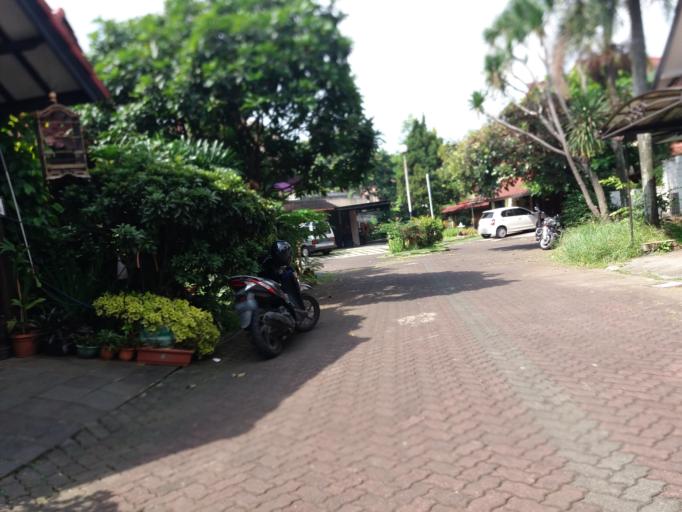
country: ID
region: West Java
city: Bandung
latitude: -6.9175
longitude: 107.6536
